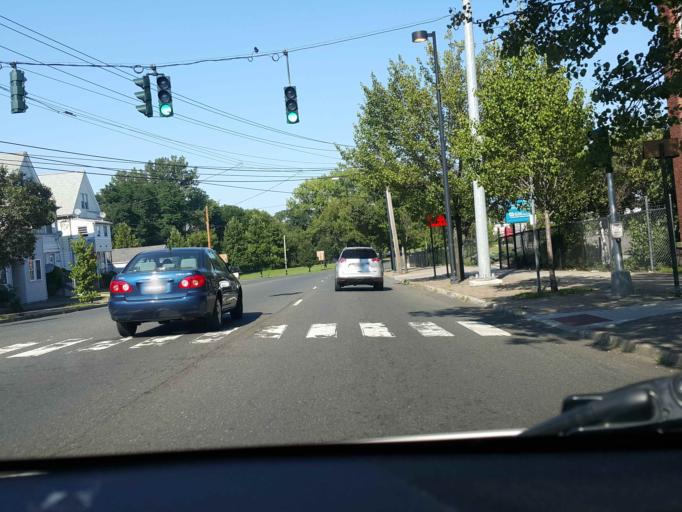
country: US
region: Connecticut
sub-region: New Haven County
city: West Haven
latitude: 41.2965
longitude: -72.9554
